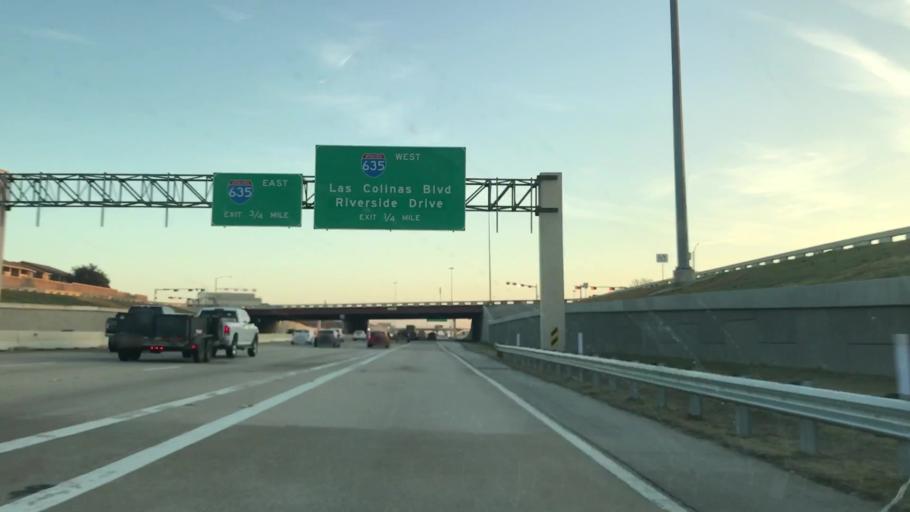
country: US
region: Texas
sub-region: Dallas County
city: Farmers Branch
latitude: 32.9031
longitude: -96.9605
